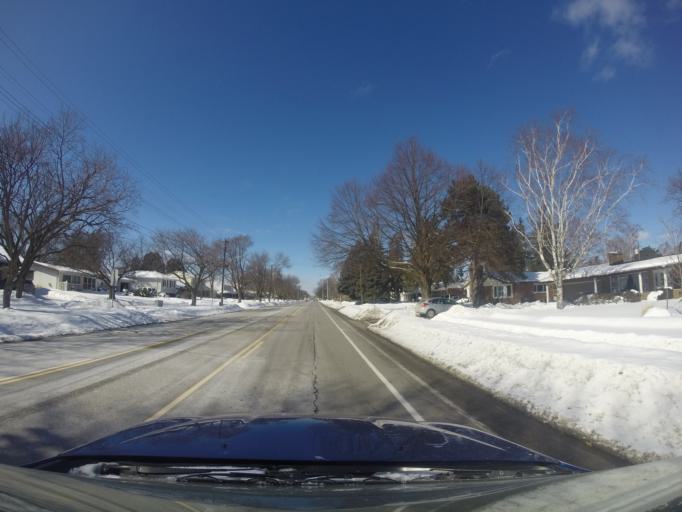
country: CA
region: Ontario
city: Burlington
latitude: 43.3503
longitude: -79.7660
